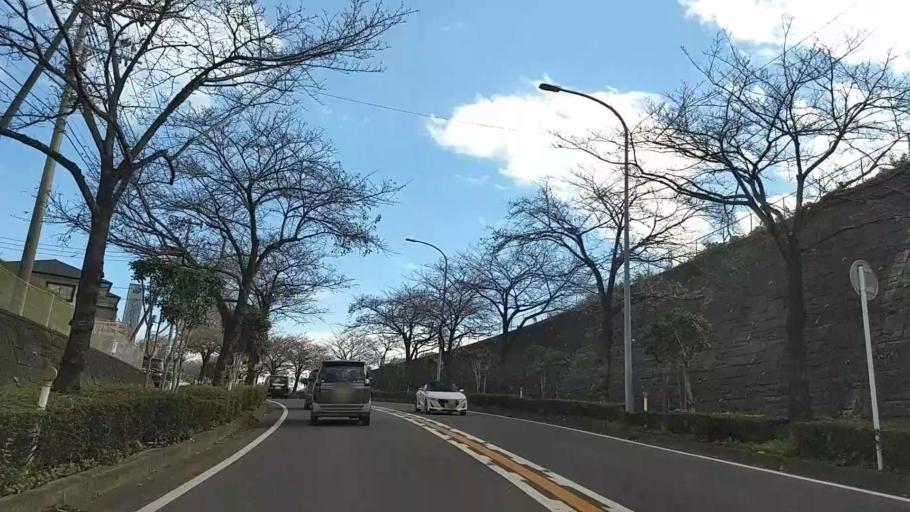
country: JP
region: Kanagawa
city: Hadano
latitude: 35.3624
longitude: 139.2165
